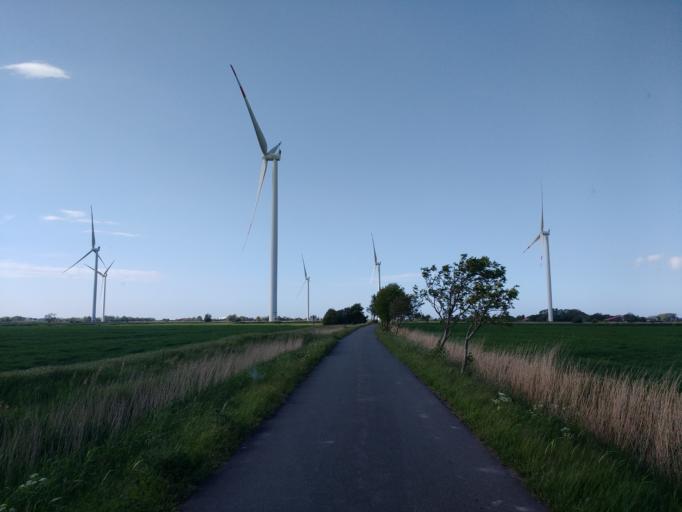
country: DE
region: Lower Saxony
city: Schillig
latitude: 53.6893
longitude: 7.9364
